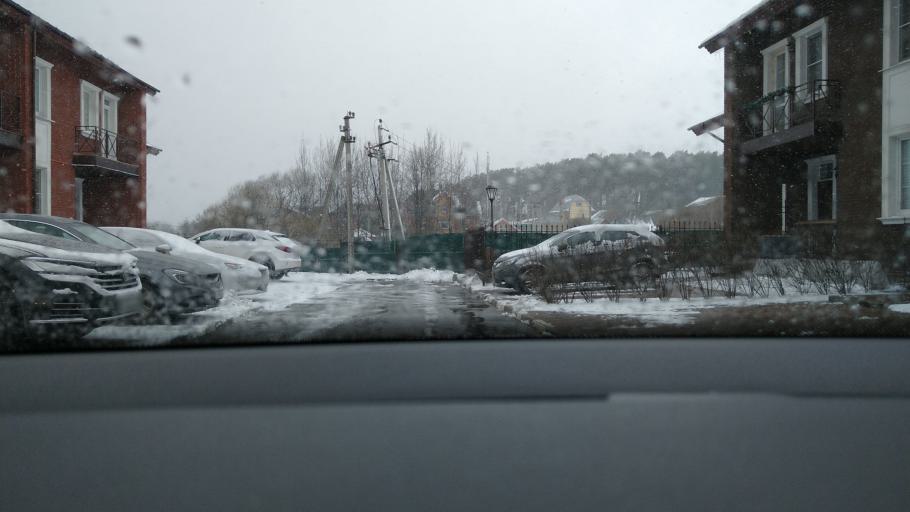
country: RU
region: Moskovskaya
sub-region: Leninskiy Rayon
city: Vnukovo
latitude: 55.6177
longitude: 37.3182
